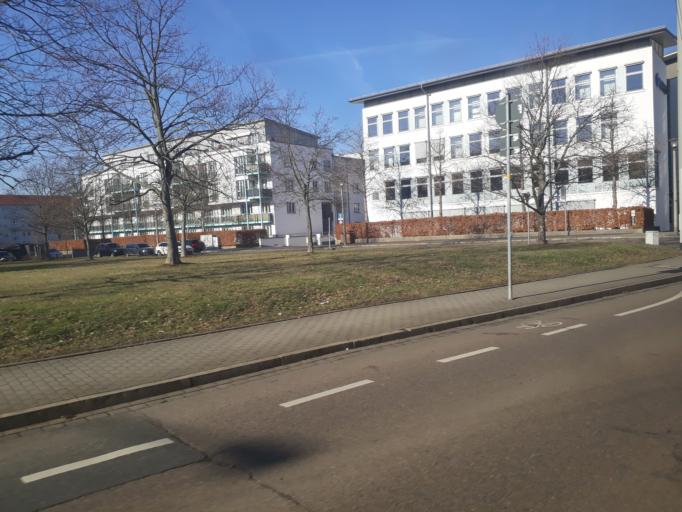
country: DE
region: Saxony
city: Heidenau
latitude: 51.0176
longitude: 13.8144
